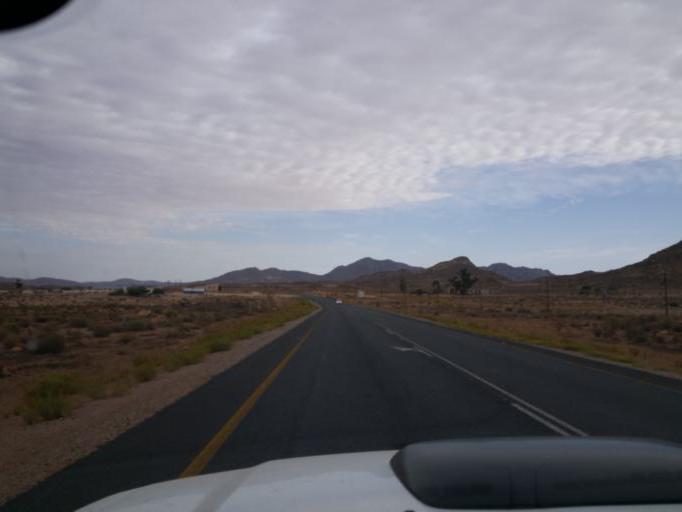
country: ZA
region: Northern Cape
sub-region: Namakwa District Municipality
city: Springbok
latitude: -29.5676
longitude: 17.8680
